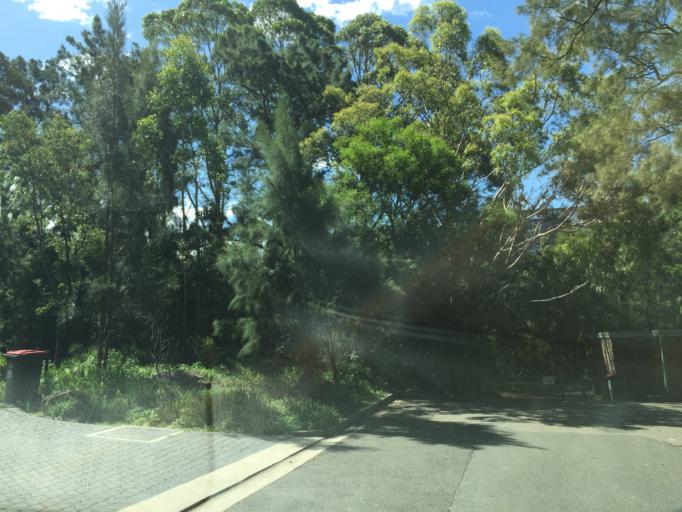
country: AU
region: New South Wales
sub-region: Lane Cove
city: Lane Cove West
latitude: -33.8007
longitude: 151.1462
